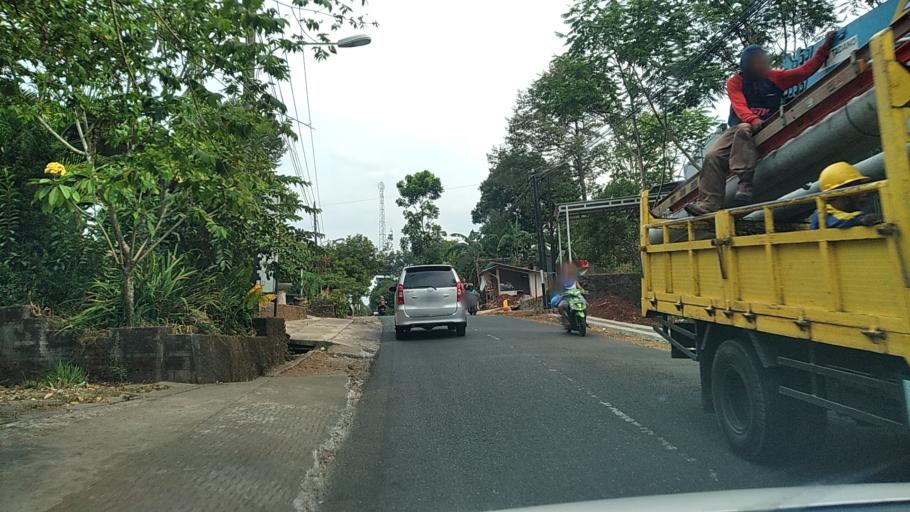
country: ID
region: Central Java
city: Ungaran
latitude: -7.0877
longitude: 110.3880
